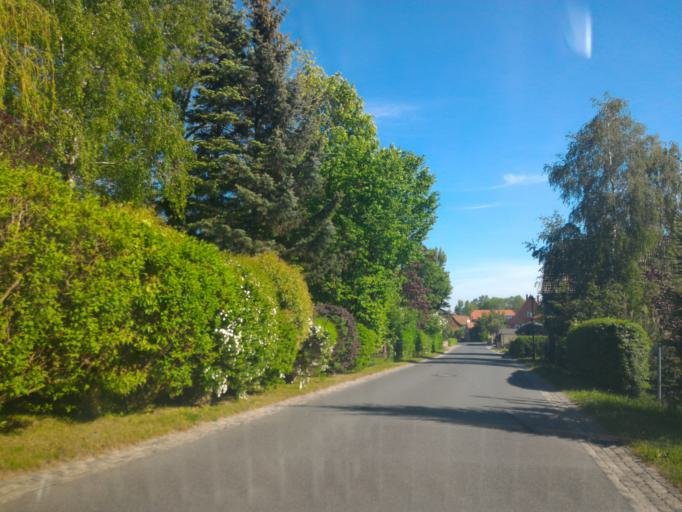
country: DE
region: Saxony
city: Niedercunnersdorf
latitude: 51.0234
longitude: 14.6765
